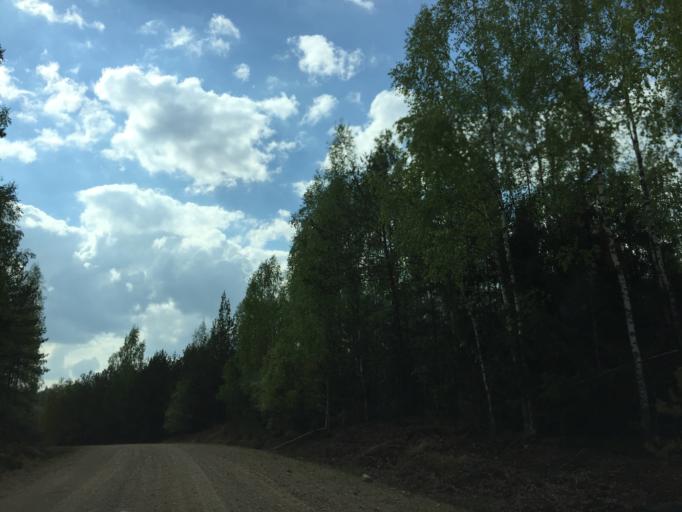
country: LV
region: Sigulda
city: Sigulda
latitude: 57.2956
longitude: 24.8348
